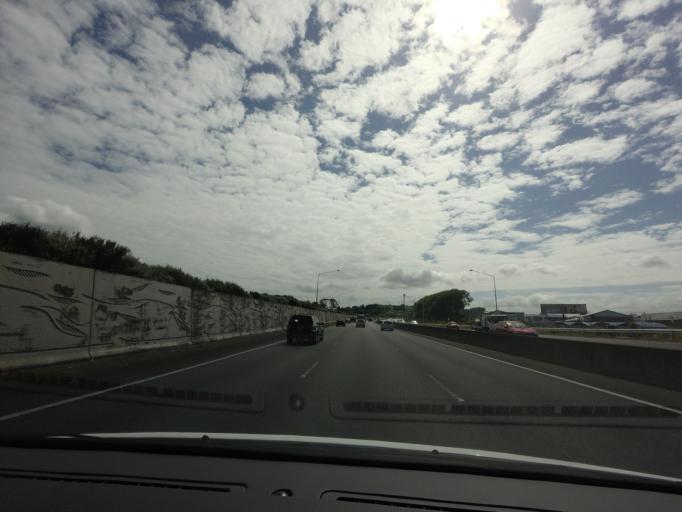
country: NZ
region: Auckland
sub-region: Auckland
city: Auckland
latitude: -36.9148
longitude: 174.7491
